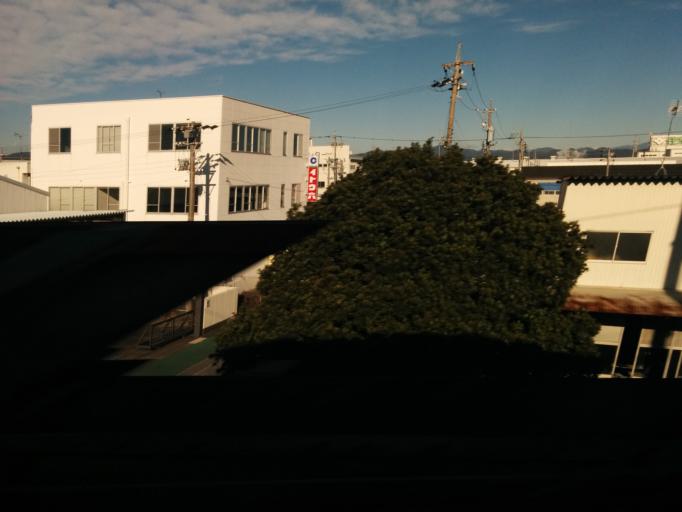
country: JP
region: Shizuoka
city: Fujieda
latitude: 34.8508
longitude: 138.2754
